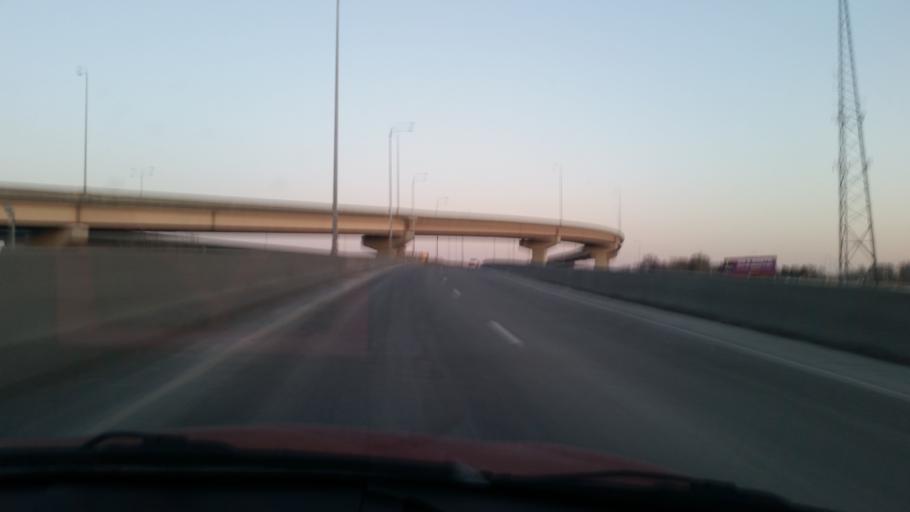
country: US
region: Nebraska
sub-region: Douglas County
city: Omaha
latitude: 41.2269
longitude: -95.9555
